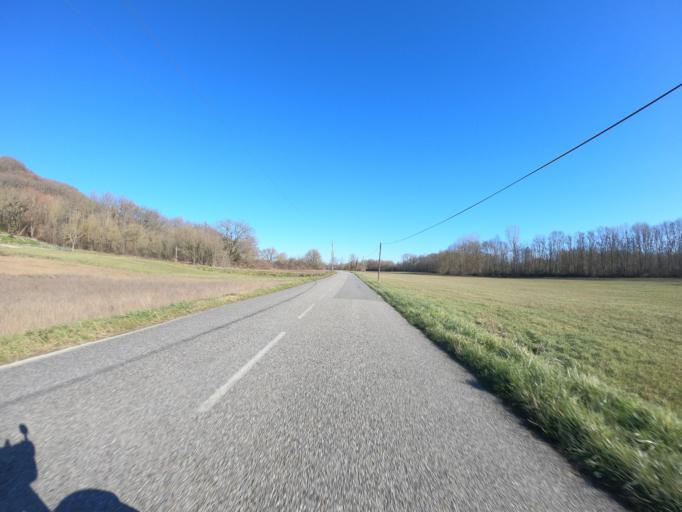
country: FR
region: Midi-Pyrenees
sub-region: Departement de l'Ariege
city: Mirepoix
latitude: 43.0868
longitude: 1.8326
